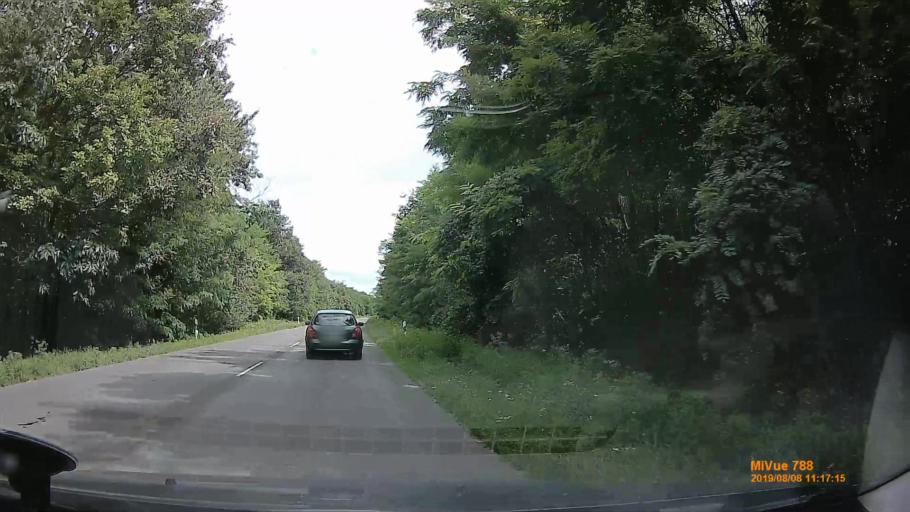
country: HU
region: Somogy
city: Balatonbereny
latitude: 46.6570
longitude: 17.3159
